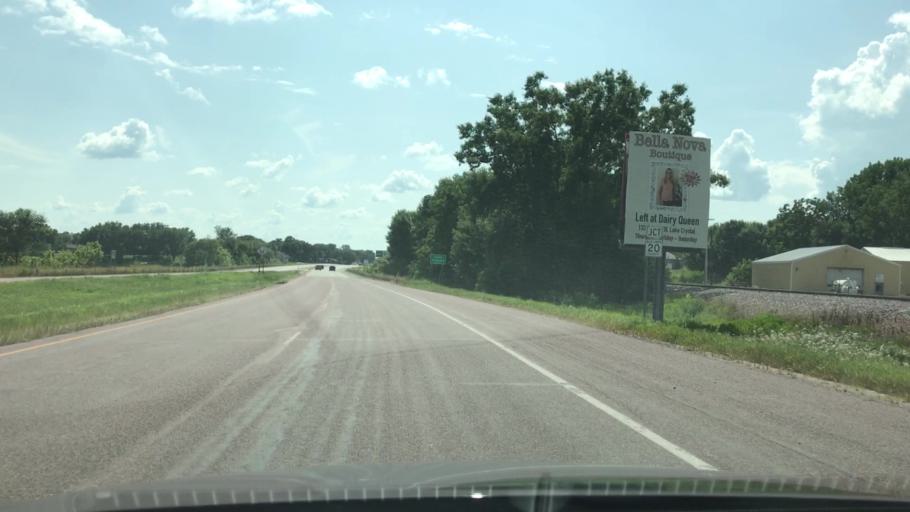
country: US
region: Minnesota
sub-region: Blue Earth County
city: Lake Crystal
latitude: 44.1164
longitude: -94.2094
